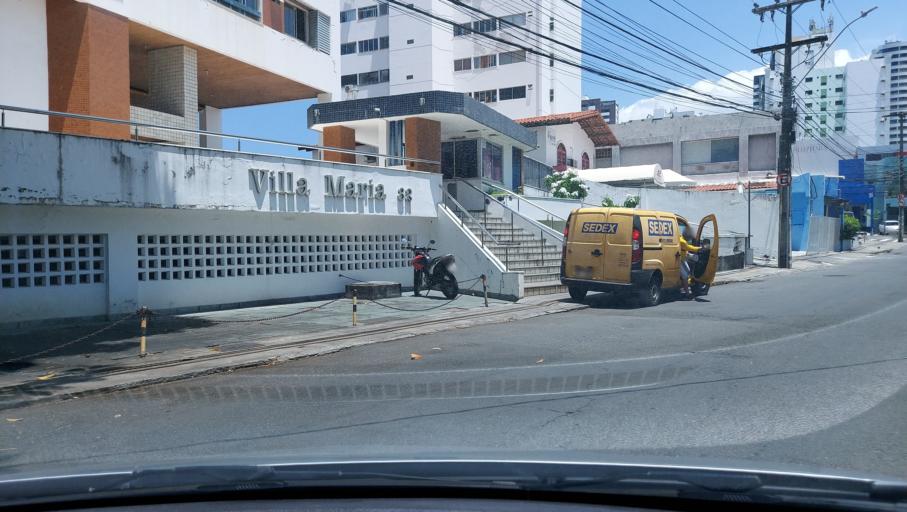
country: BR
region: Bahia
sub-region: Salvador
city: Salvador
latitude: -12.9924
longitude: -38.4539
